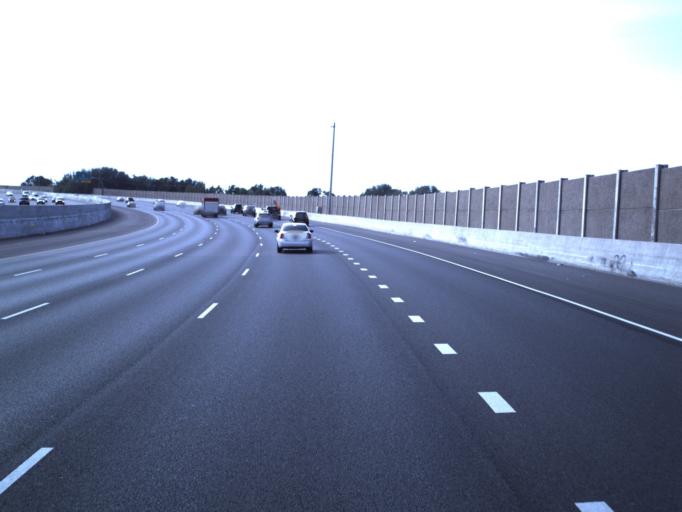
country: US
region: Utah
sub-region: Salt Lake County
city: Taylorsville
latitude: 40.6435
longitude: -111.9274
